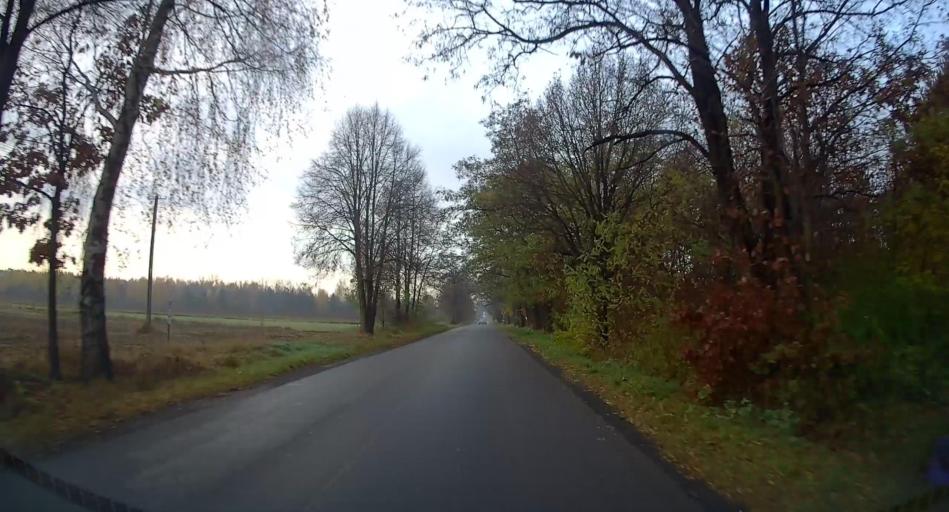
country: PL
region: Masovian Voivodeship
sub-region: Powiat zyrardowski
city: Puszcza Marianska
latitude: 51.9314
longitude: 20.3621
